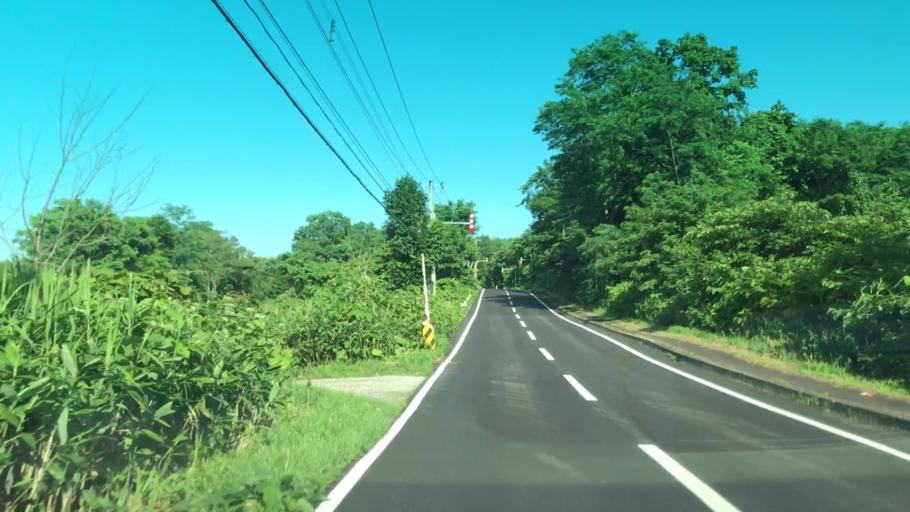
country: JP
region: Hokkaido
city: Yoichi
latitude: 43.0325
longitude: 140.7669
